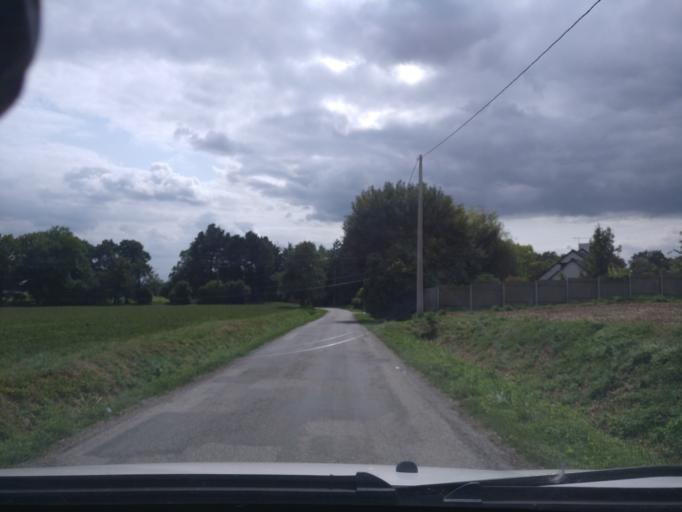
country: FR
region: Brittany
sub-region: Departement d'Ille-et-Vilaine
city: Noyal-sur-Vilaine
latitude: 48.0802
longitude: -1.5326
